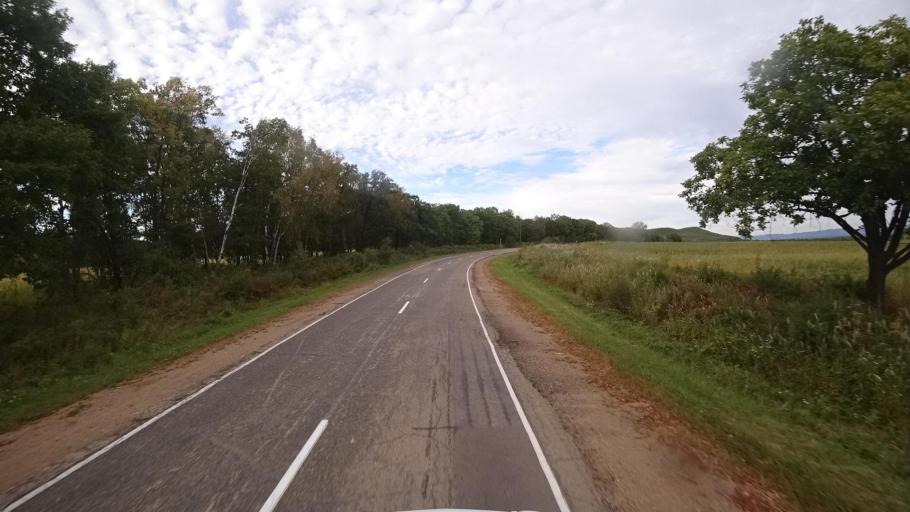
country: RU
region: Primorskiy
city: Dostoyevka
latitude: 44.3708
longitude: 133.4345
